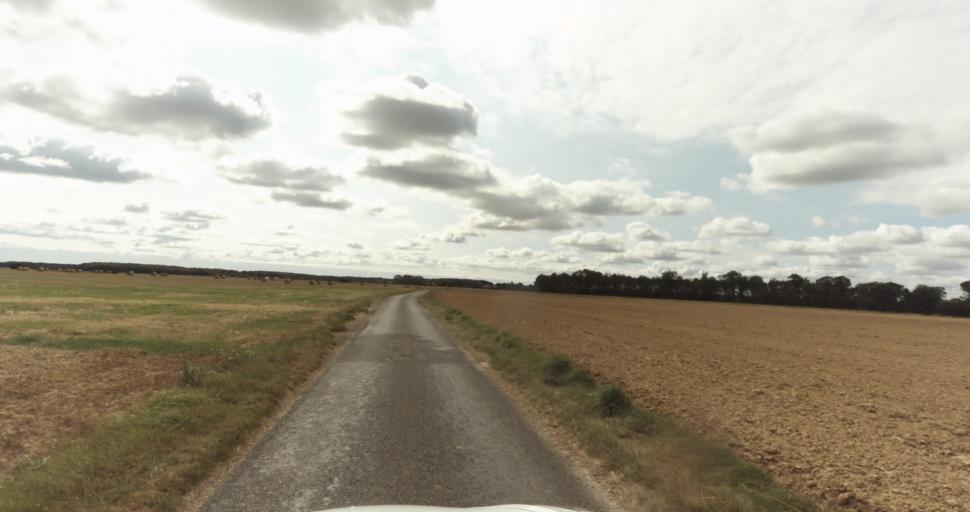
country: FR
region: Haute-Normandie
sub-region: Departement de l'Eure
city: Tillieres-sur-Avre
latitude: 48.7885
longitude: 1.1002
